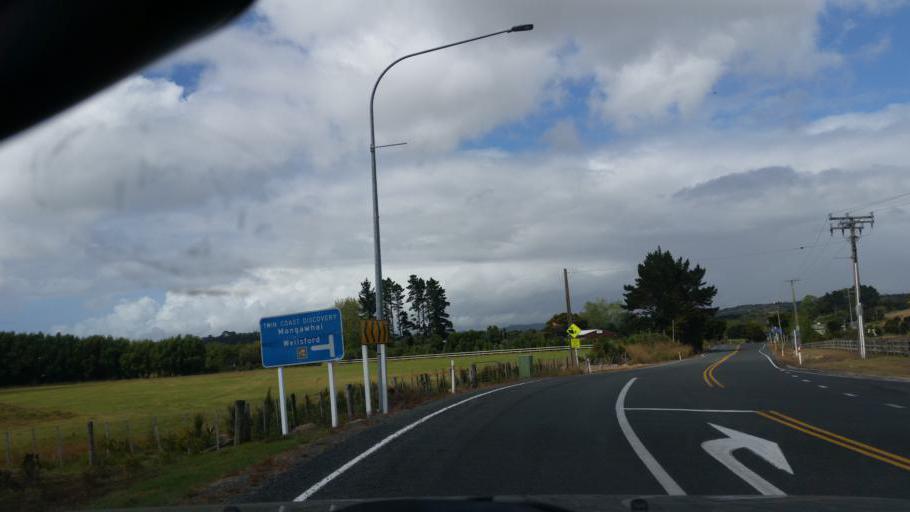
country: NZ
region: Auckland
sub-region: Auckland
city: Wellsford
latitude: -36.0801
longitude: 174.5718
